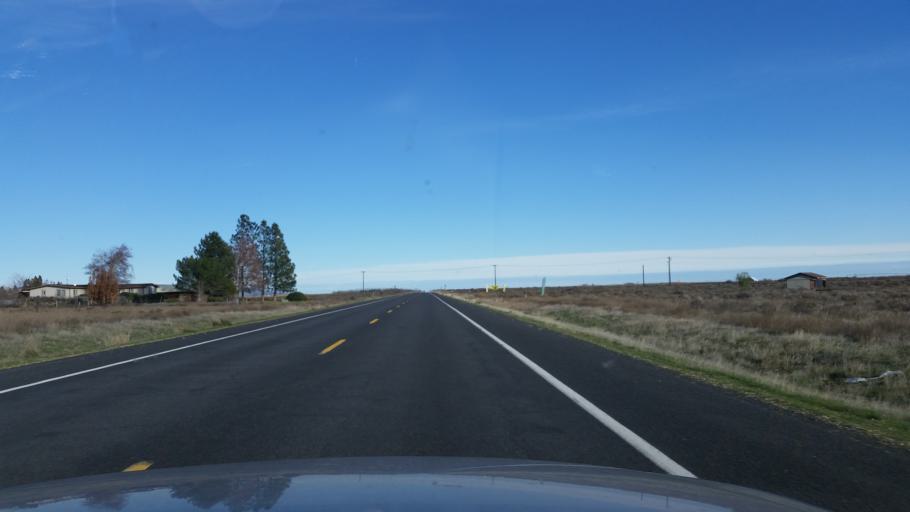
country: US
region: Washington
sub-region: Grant County
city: Quincy
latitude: 47.1677
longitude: -119.7288
